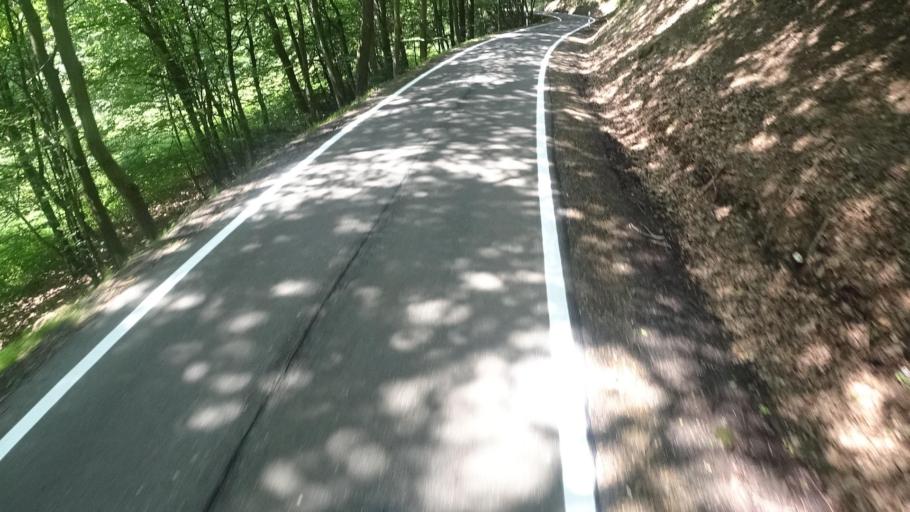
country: DE
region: Rheinland-Pfalz
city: Sankt Katharinen
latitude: 50.5814
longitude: 7.3555
